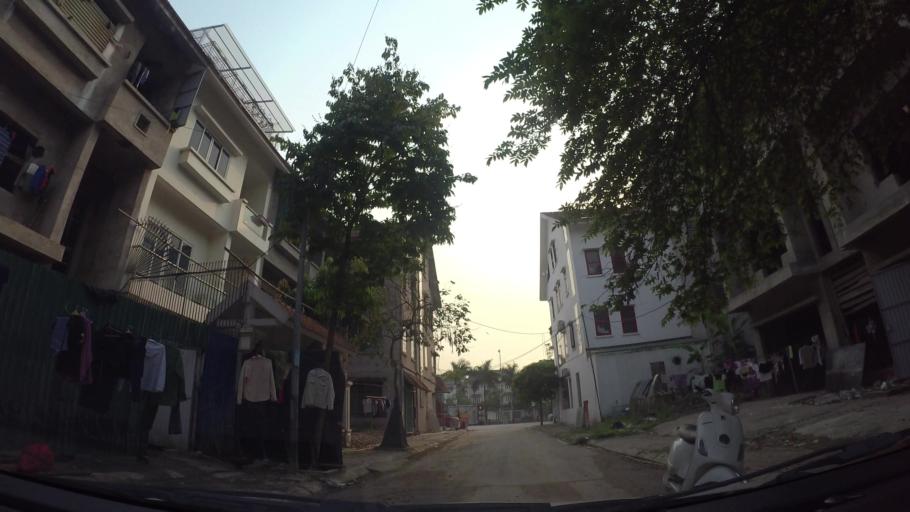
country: VN
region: Ha Noi
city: Cau Dien
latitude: 21.0012
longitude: 105.7341
